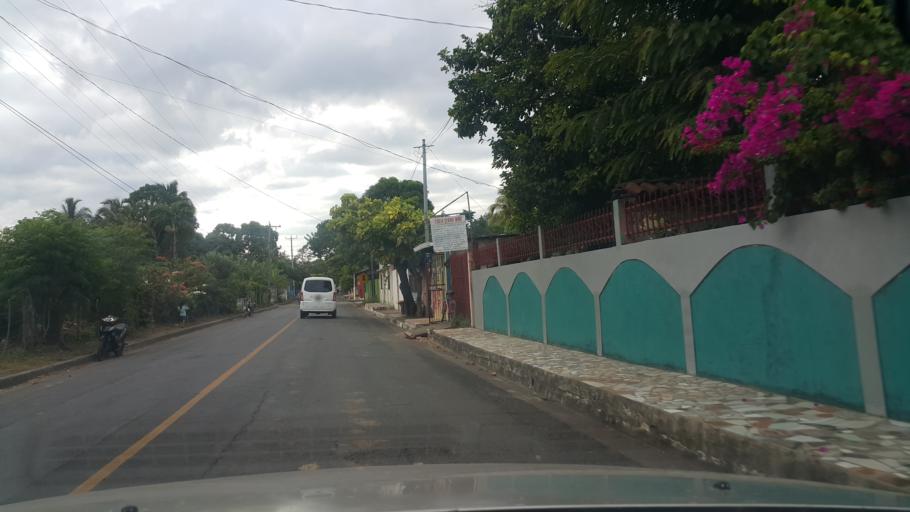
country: NI
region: Rivas
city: Moyogalpa
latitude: 11.4962
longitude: -85.6926
